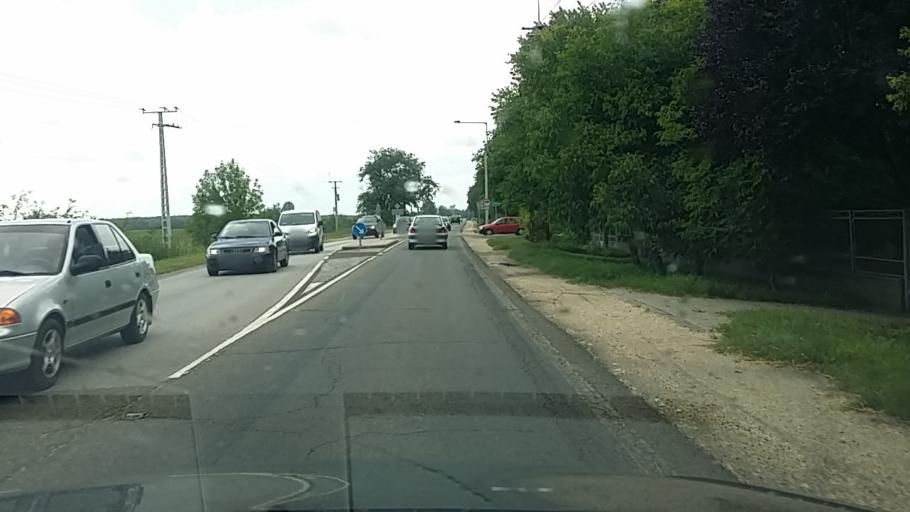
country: HU
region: Pest
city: Orkeny
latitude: 47.1344
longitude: 19.4136
